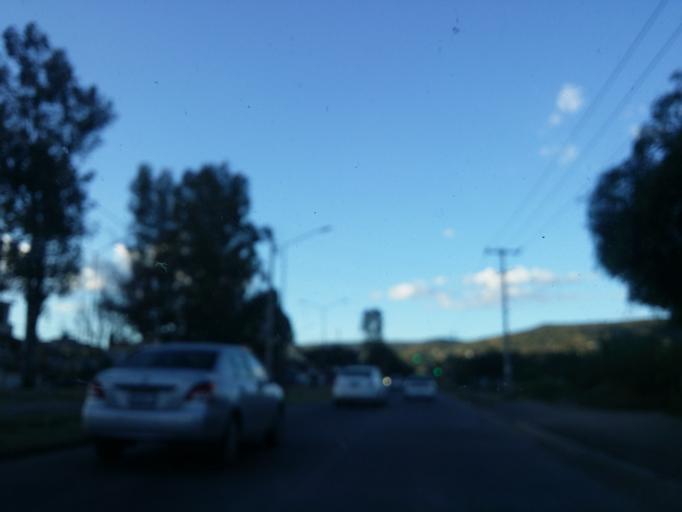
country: MX
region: Guanajuato
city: Leon
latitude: 21.1773
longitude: -101.6641
